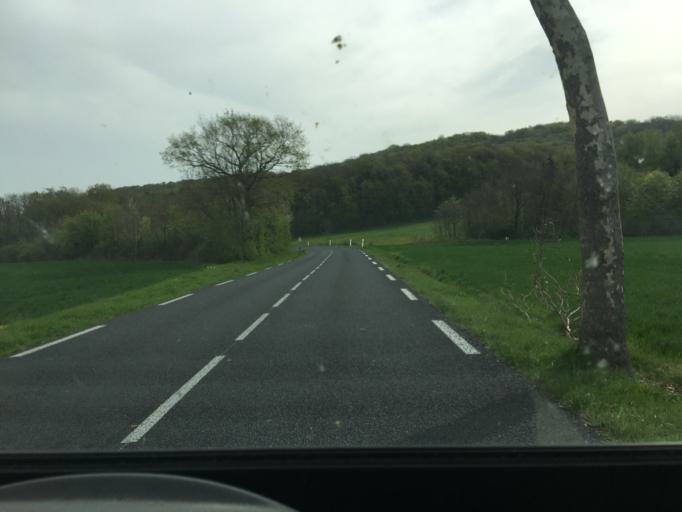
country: FR
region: Lorraine
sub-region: Departement de Meurthe-et-Moselle
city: Einville-au-Jard
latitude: 48.7029
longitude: 6.5047
